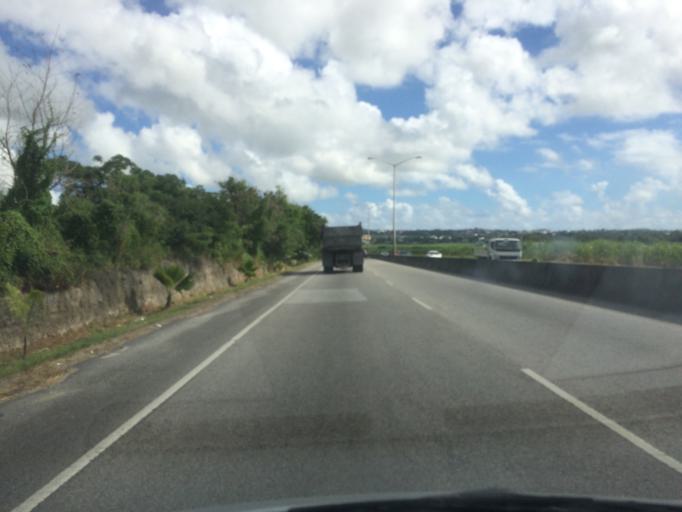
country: BB
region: Saint Michael
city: Bridgetown
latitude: 13.1220
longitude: -59.5910
